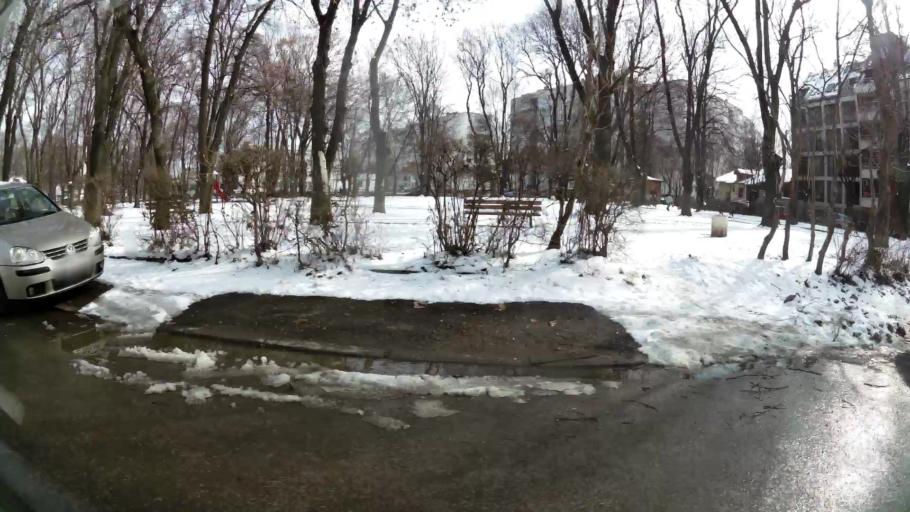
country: BG
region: Sofia-Capital
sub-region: Stolichna Obshtina
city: Sofia
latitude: 42.7066
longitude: 23.3437
